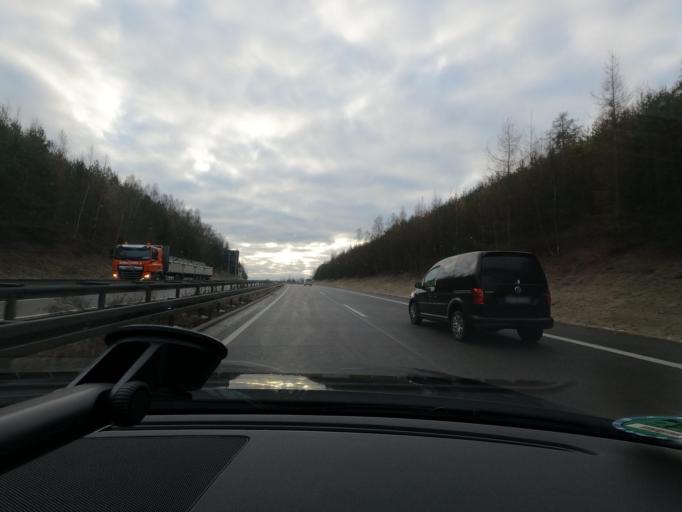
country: DE
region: Thuringia
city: Schleusingen
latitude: 50.5051
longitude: 10.7807
